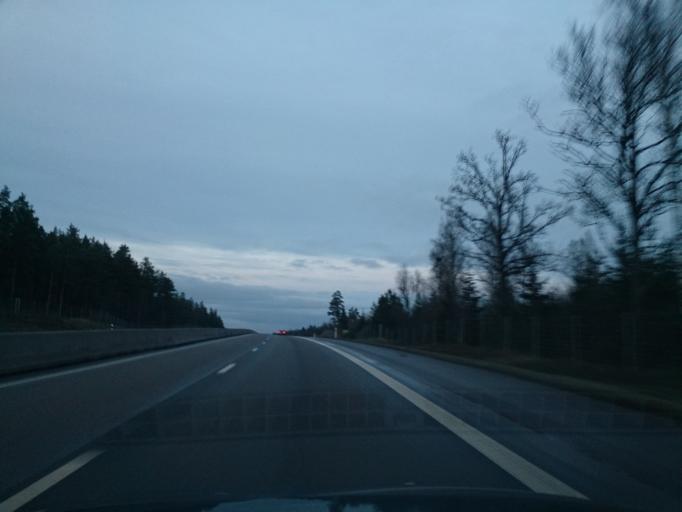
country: SE
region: OEstergoetland
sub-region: Norrkopings Kommun
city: Kimstad
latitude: 58.5359
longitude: 16.0385
